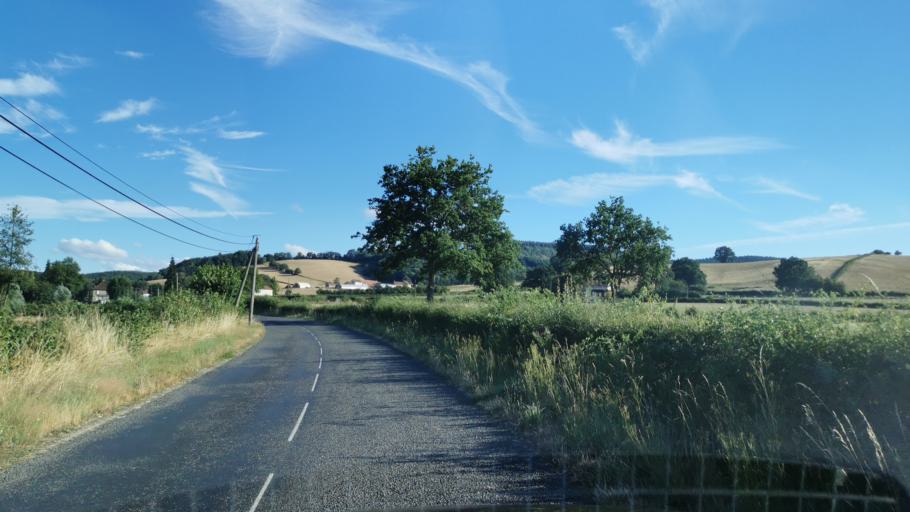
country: FR
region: Bourgogne
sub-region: Departement de Saone-et-Loire
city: Marmagne
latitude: 46.8069
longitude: 4.3280
